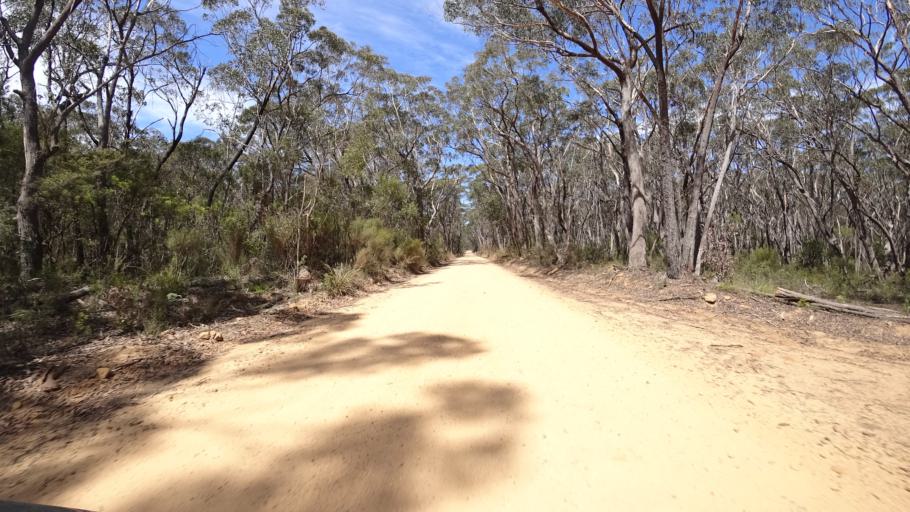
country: AU
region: New South Wales
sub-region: Lithgow
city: Lithgow
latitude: -33.2811
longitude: 150.2328
